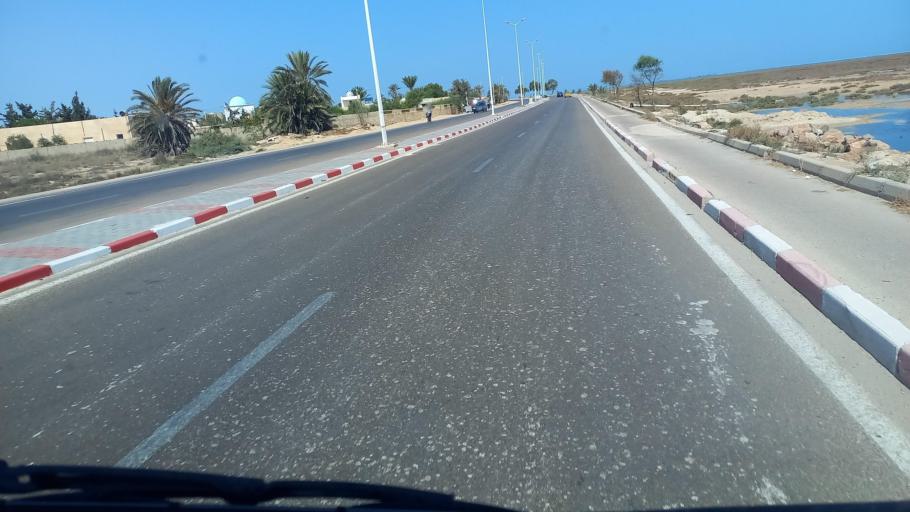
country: TN
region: Madanin
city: Houmt Souk
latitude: 33.8703
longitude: 10.9374
